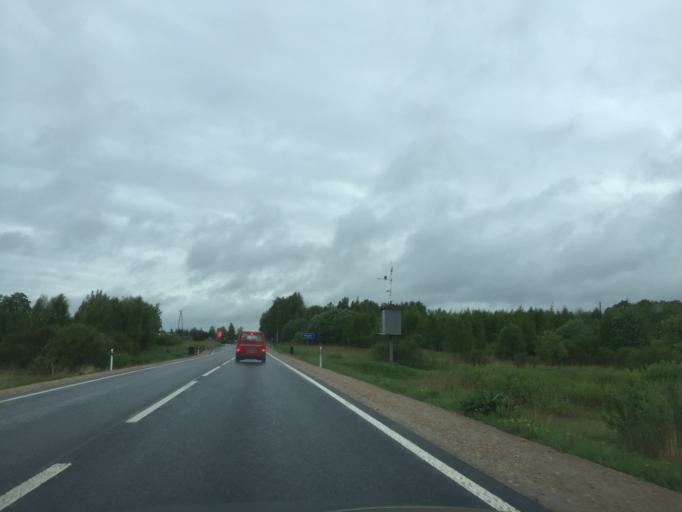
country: LV
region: Ogre
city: Jumprava
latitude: 56.6601
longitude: 24.8979
